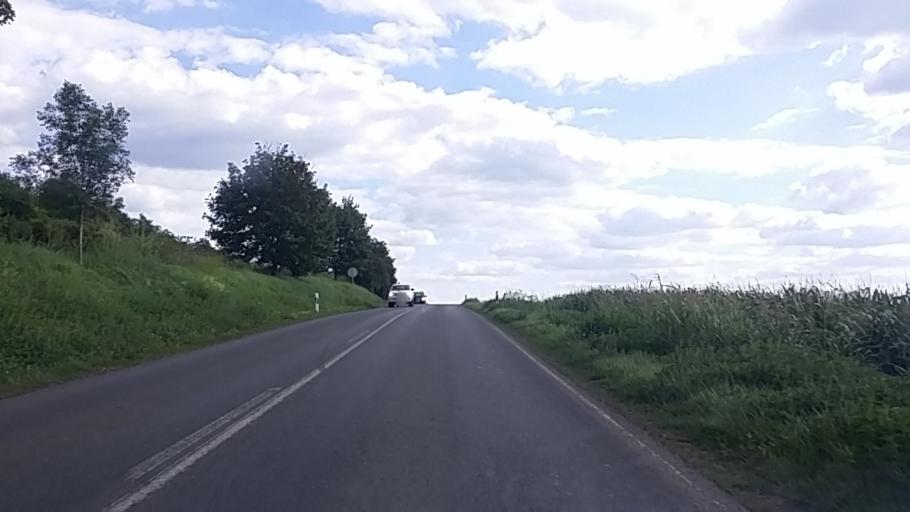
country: HU
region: Baranya
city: Sasd
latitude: 46.2366
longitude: 18.1212
